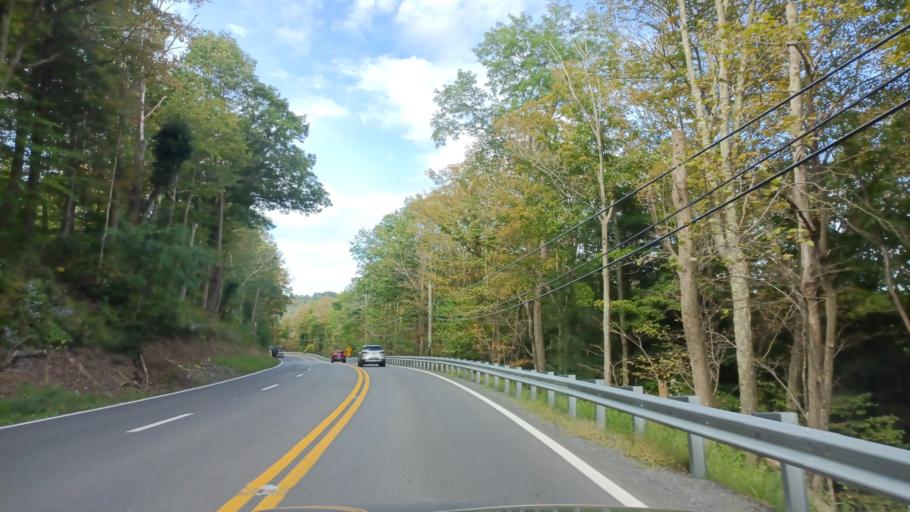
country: US
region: Maryland
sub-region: Garrett County
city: Mountain Lake Park
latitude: 39.2963
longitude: -79.3330
